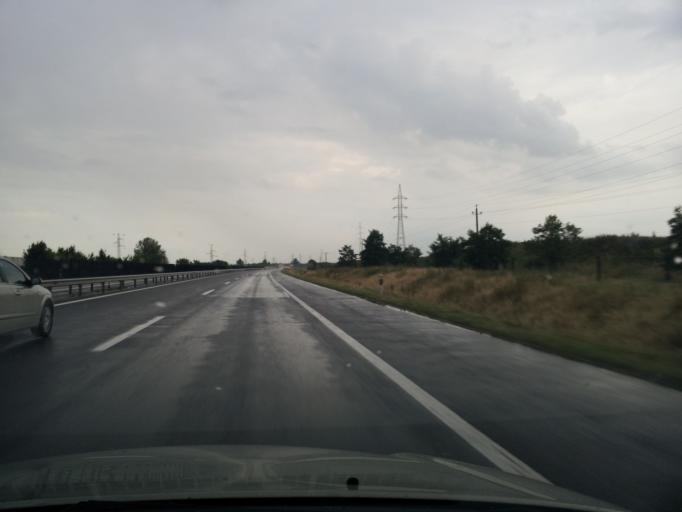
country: HU
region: Borsod-Abauj-Zemplen
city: Onod
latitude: 47.9911
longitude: 20.8944
